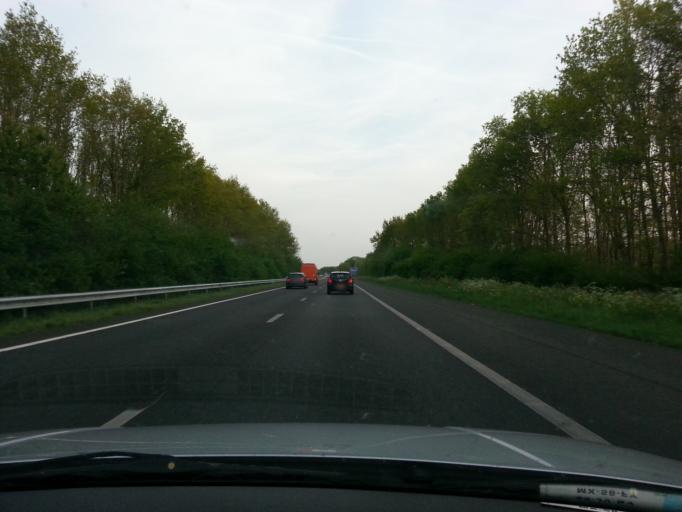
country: NL
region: Flevoland
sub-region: Gemeente Noordoostpolder
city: Emmeloord
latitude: 52.7438
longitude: 5.7685
